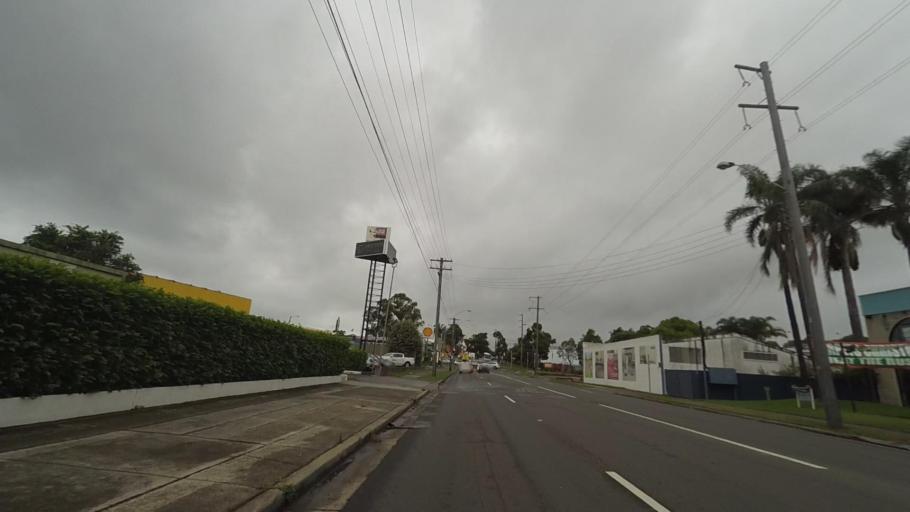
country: AU
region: New South Wales
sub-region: Sutherland Shire
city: Caringbah
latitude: -34.0267
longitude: 151.1192
